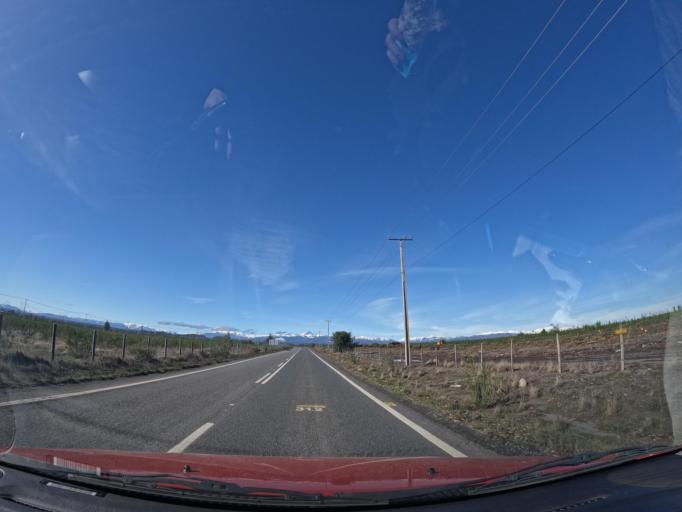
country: CL
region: Biobio
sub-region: Provincia de Biobio
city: Los Angeles
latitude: -37.4157
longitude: -71.9870
